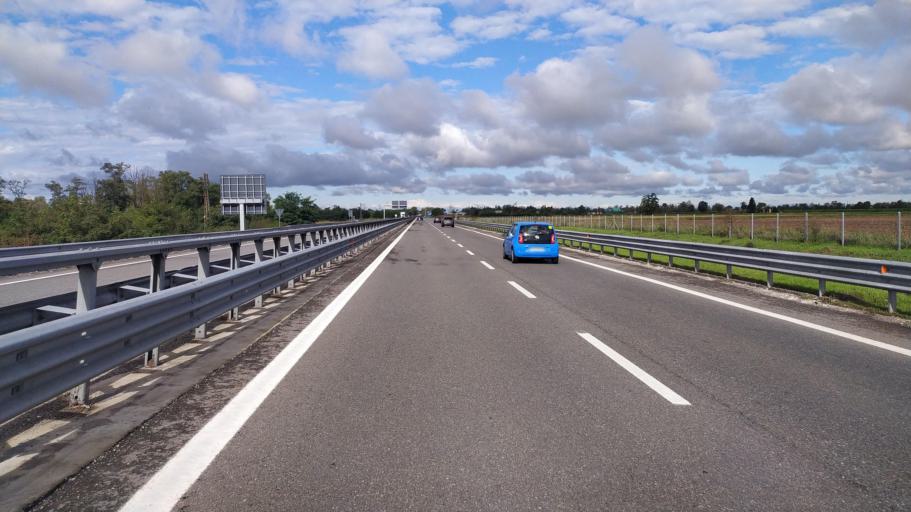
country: IT
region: Lombardy
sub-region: Provincia di Pavia
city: Pavia
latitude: 45.2005
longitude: 9.1213
